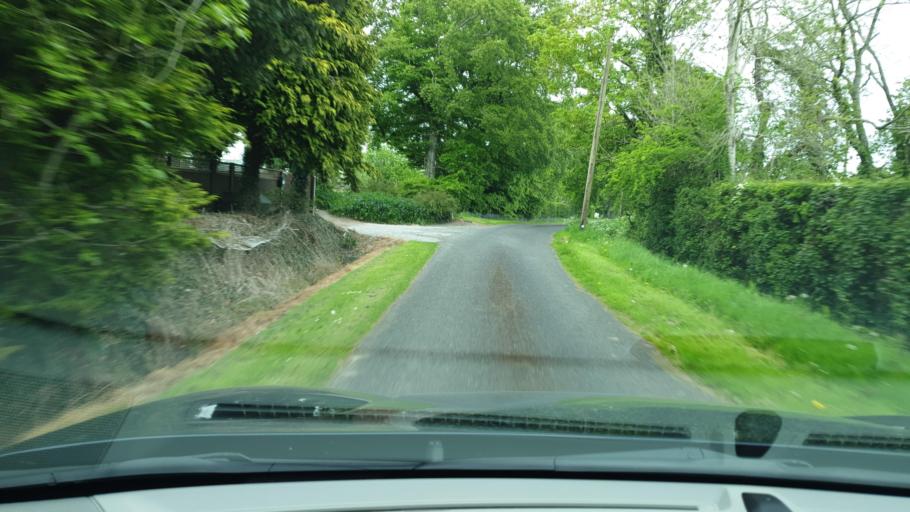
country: IE
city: Confey
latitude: 53.4193
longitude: -6.5312
